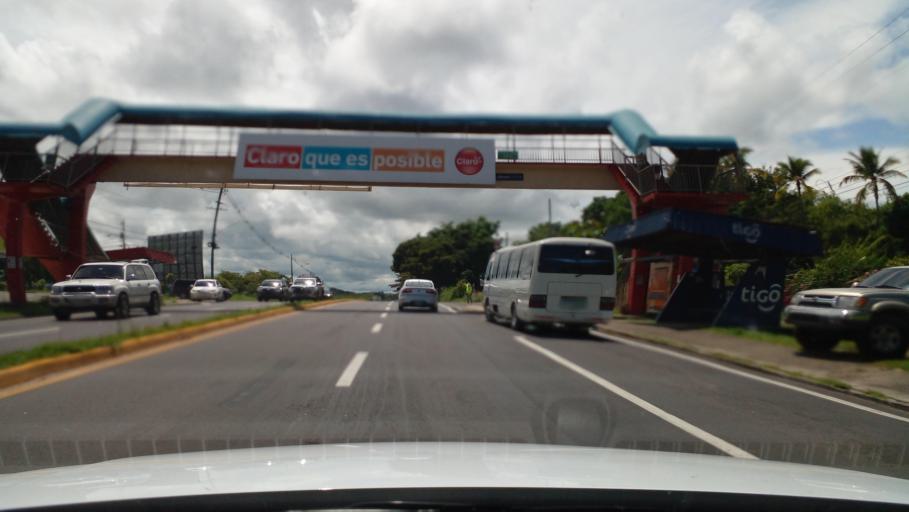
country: PA
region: Cocle
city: Rio Hato
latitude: 8.4268
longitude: -80.0711
